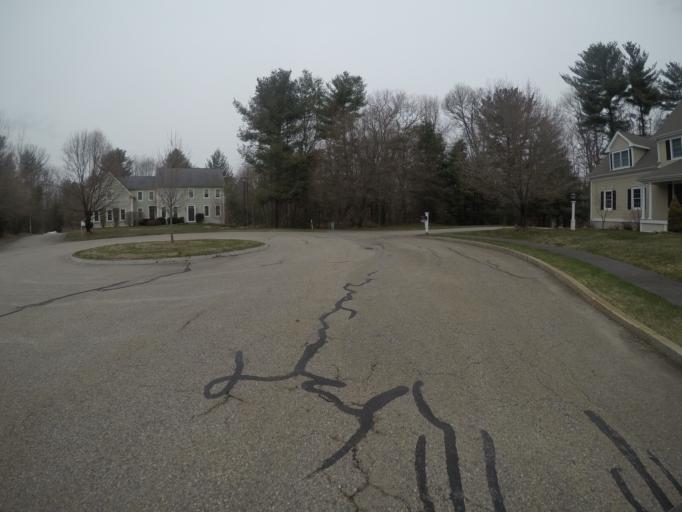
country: US
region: Massachusetts
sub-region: Bristol County
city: Easton
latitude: 42.0332
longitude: -71.1501
